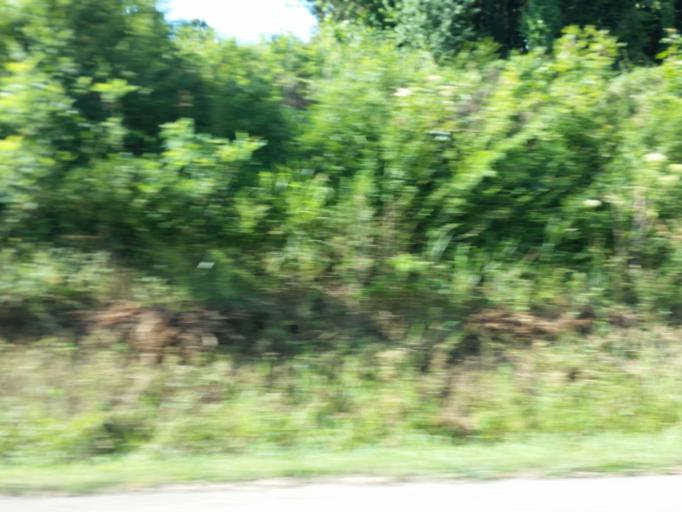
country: US
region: Tennessee
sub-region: Perry County
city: Linden
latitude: 35.6175
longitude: -87.8457
